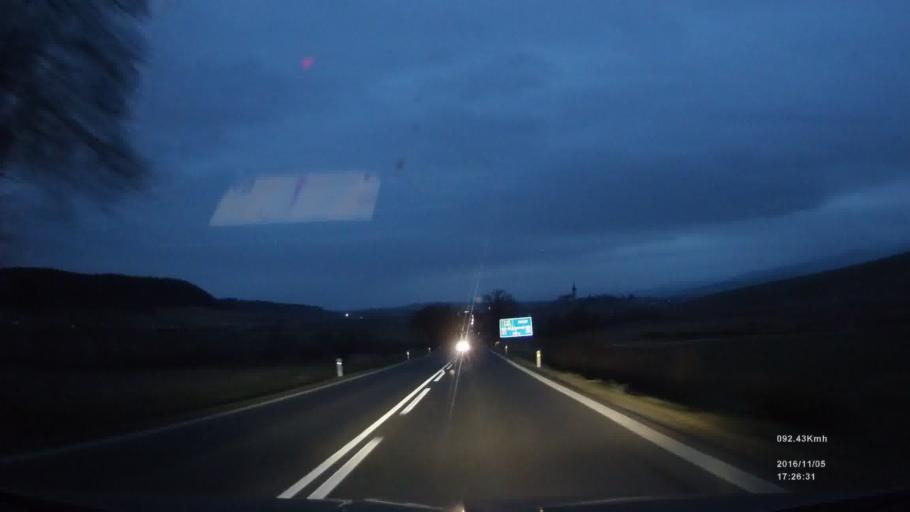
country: SK
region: Presovsky
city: Lubica
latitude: 49.0139
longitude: 20.4472
